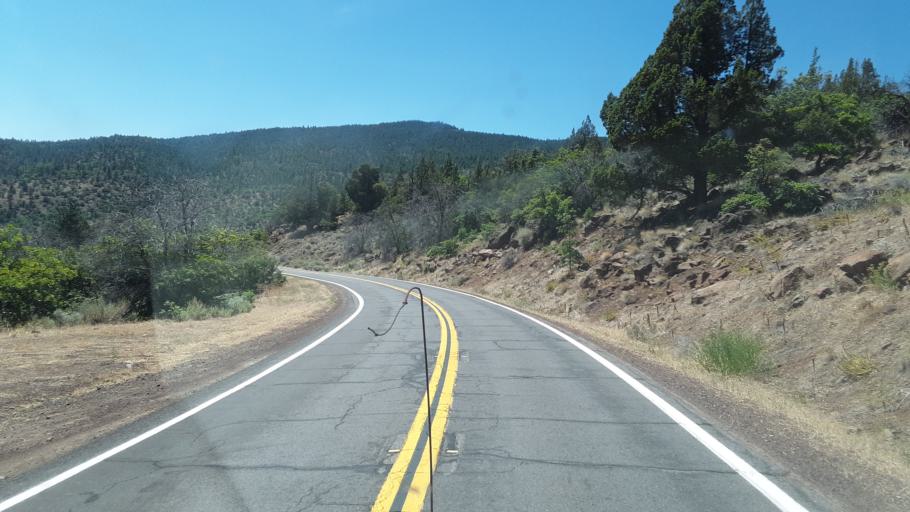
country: US
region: California
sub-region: Lassen County
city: Susanville
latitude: 40.4660
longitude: -120.6045
